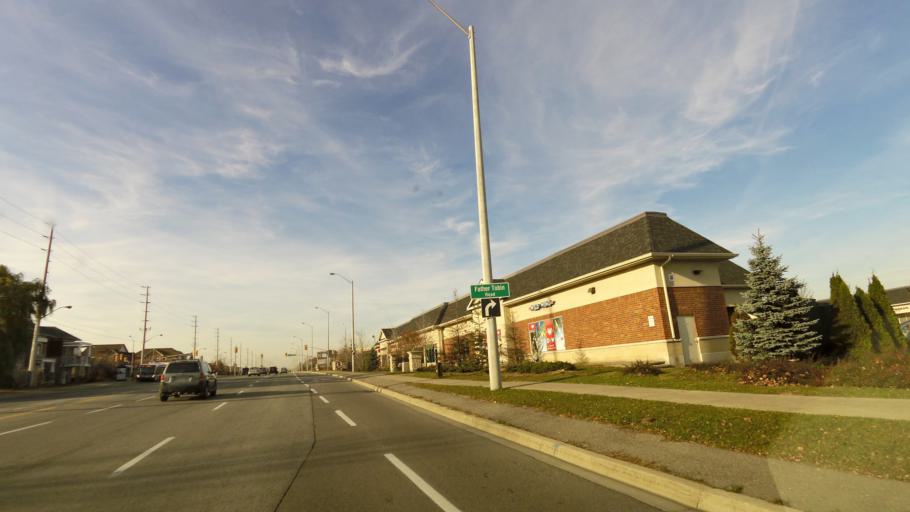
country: CA
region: Ontario
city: Brampton
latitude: 43.7702
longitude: -79.7552
